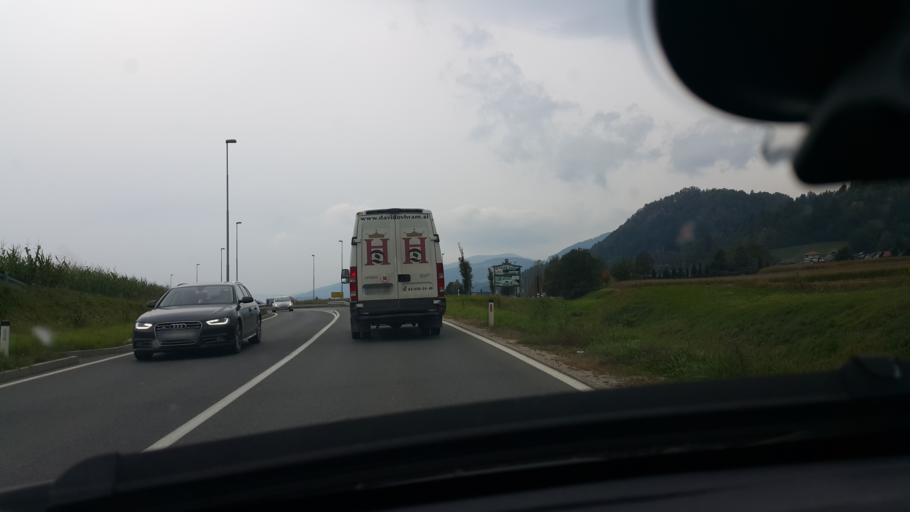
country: SI
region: Radlje ob Dravi
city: Radlje ob Dravi
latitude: 46.6117
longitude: 15.2377
